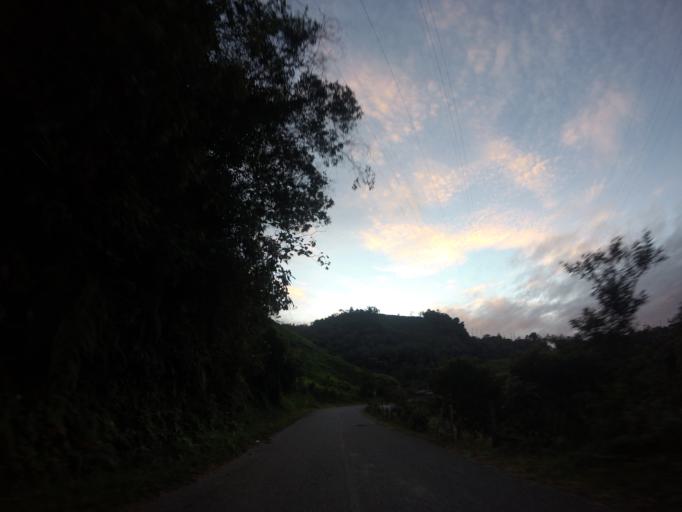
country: CO
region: Caldas
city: Manzanares
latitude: 5.2707
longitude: -75.1251
